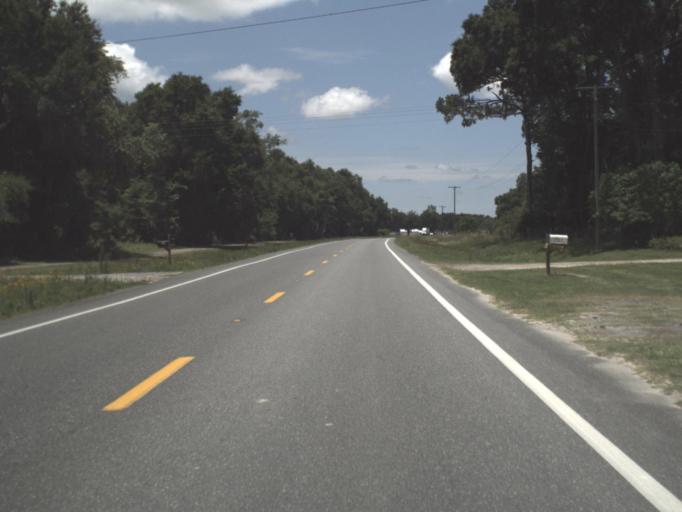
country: US
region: Florida
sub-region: Suwannee County
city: Wellborn
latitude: 29.9525
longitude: -82.8975
